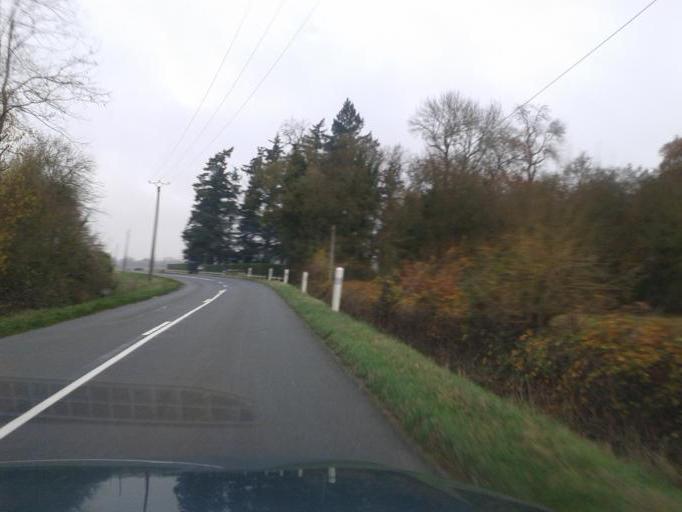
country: FR
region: Centre
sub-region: Departement du Loiret
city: Beaugency
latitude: 47.7629
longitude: 1.6428
